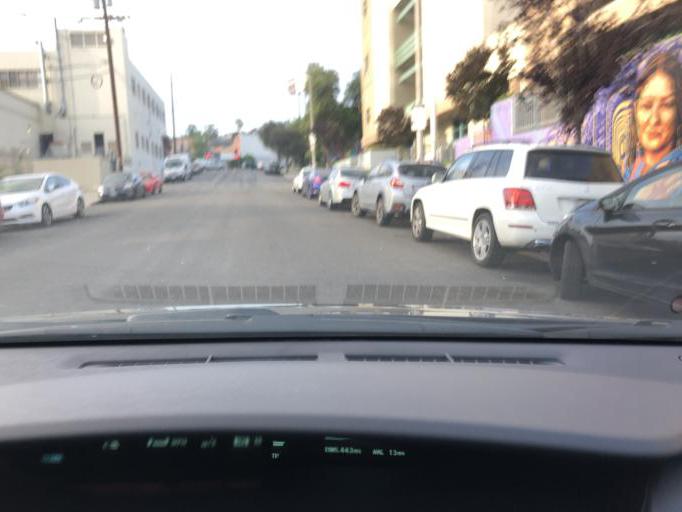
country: US
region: California
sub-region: Los Angeles County
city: Echo Park
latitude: 34.0766
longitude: -118.2655
